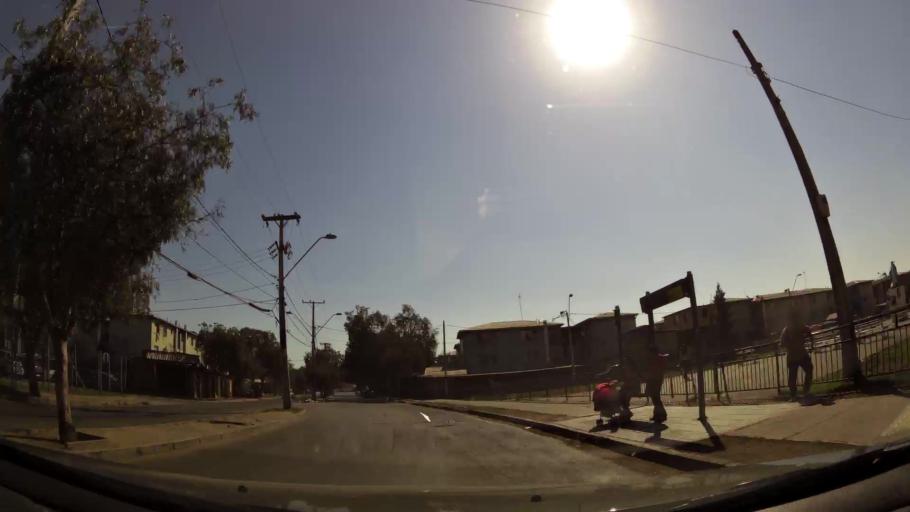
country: CL
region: Santiago Metropolitan
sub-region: Provincia de Santiago
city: La Pintana
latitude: -33.6254
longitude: -70.6262
